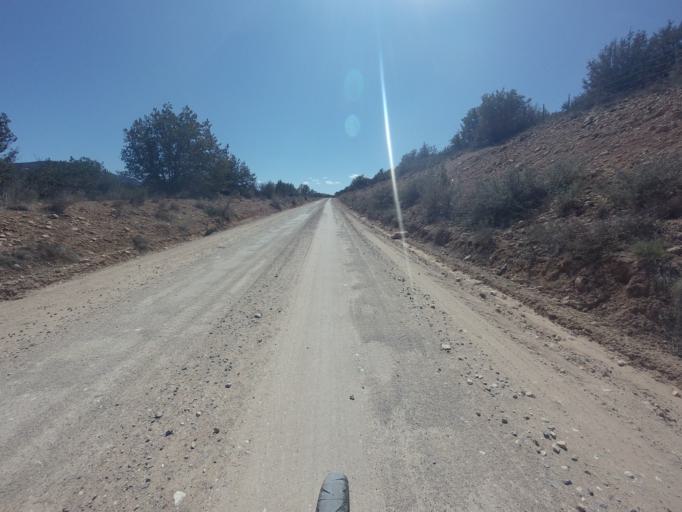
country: US
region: Arizona
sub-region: Yavapai County
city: Lake Montezuma
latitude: 34.6404
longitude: -111.7190
